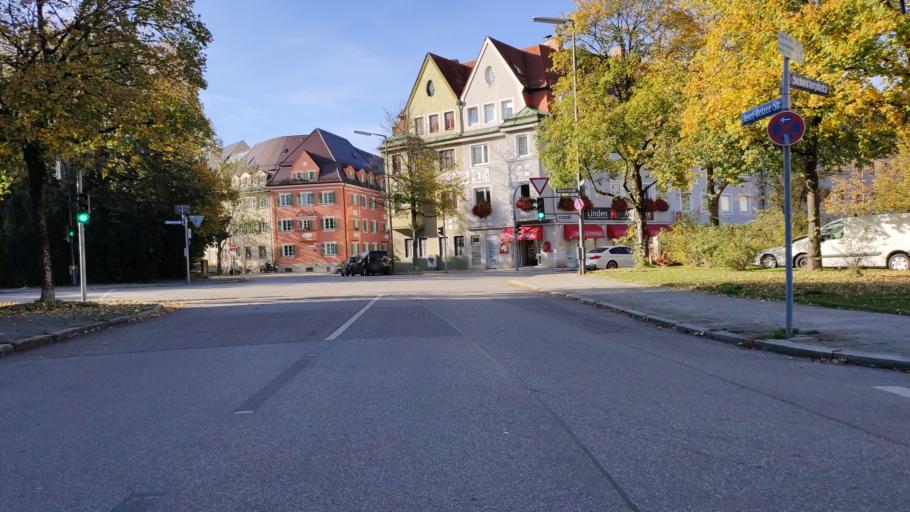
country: DE
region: Bavaria
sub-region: Upper Bavaria
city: Pasing
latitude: 48.1439
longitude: 11.4615
